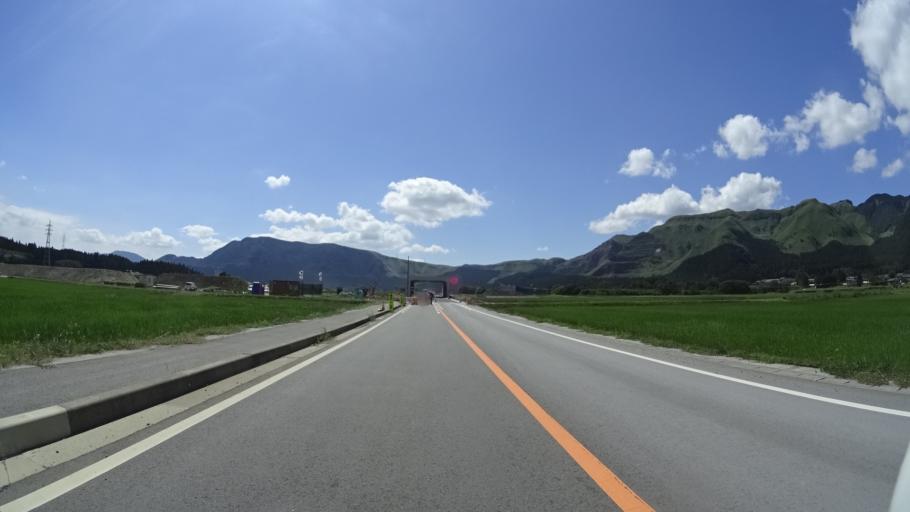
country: JP
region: Kumamoto
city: Aso
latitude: 32.9257
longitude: 130.9974
